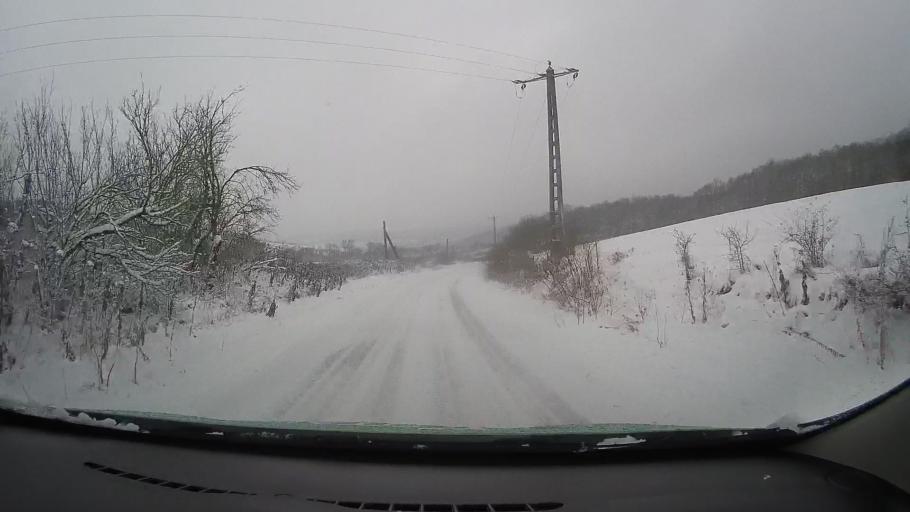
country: RO
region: Hunedoara
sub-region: Comuna Carjiti
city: Carjiti
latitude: 45.8377
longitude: 22.8373
